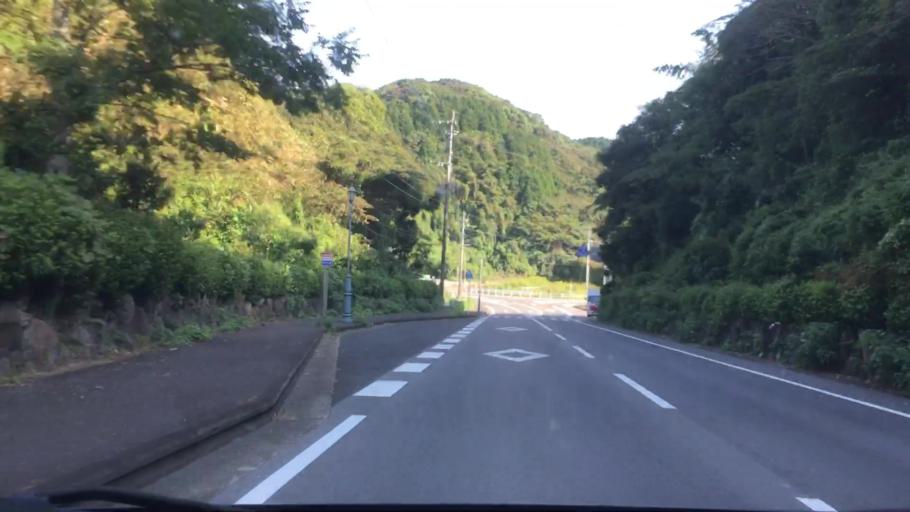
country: JP
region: Nagasaki
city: Sasebo
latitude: 33.0229
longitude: 129.6542
